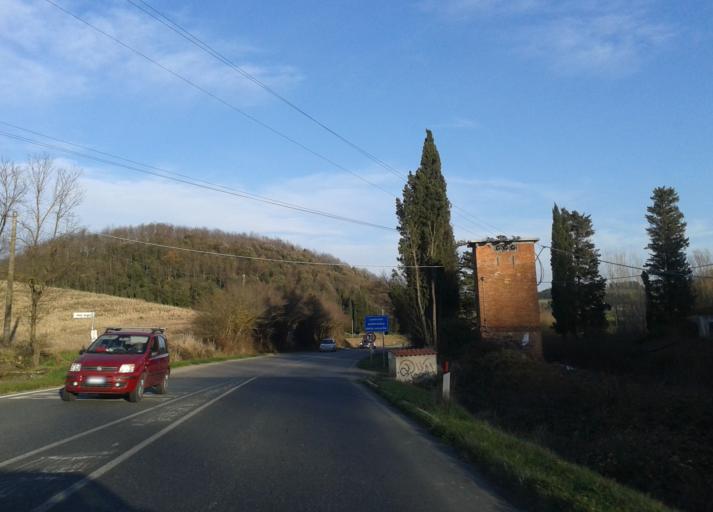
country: IT
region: Tuscany
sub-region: Provincia di Livorno
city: Guasticce
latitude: 43.5688
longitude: 10.4197
